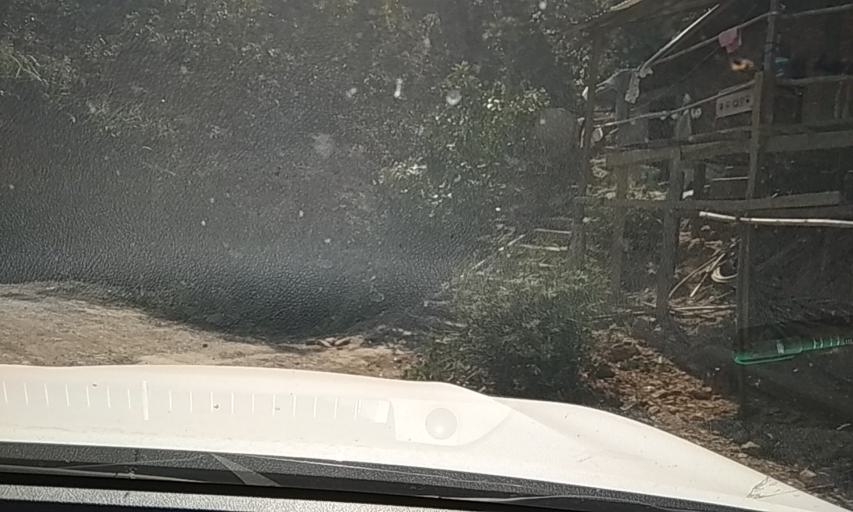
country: LA
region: Phongsali
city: Phongsali
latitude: 21.6593
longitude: 102.0910
